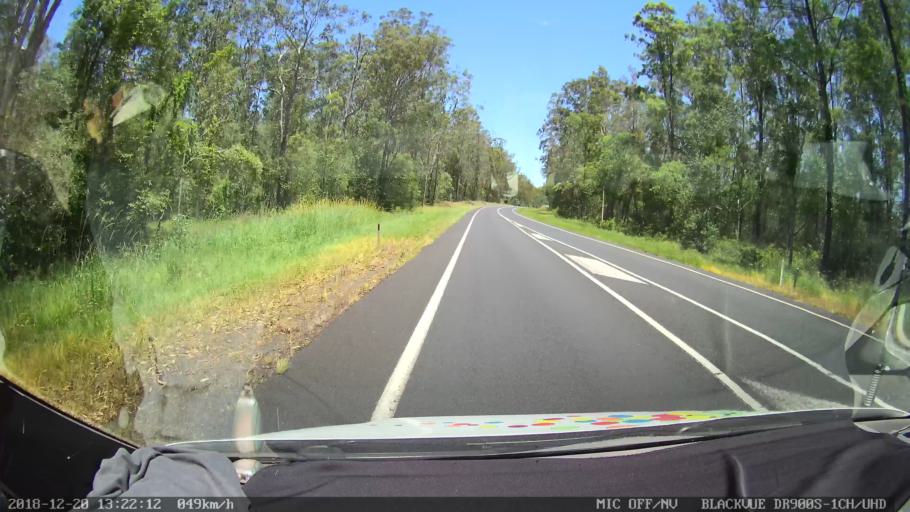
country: AU
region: New South Wales
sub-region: Richmond Valley
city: Casino
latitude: -29.0897
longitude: 153.0015
